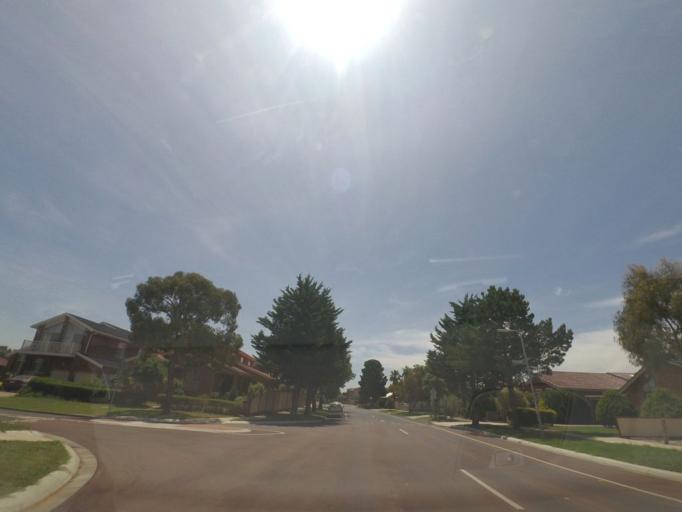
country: AU
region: Victoria
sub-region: Brimbank
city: Keilor Downs
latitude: -37.7191
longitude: 144.8030
